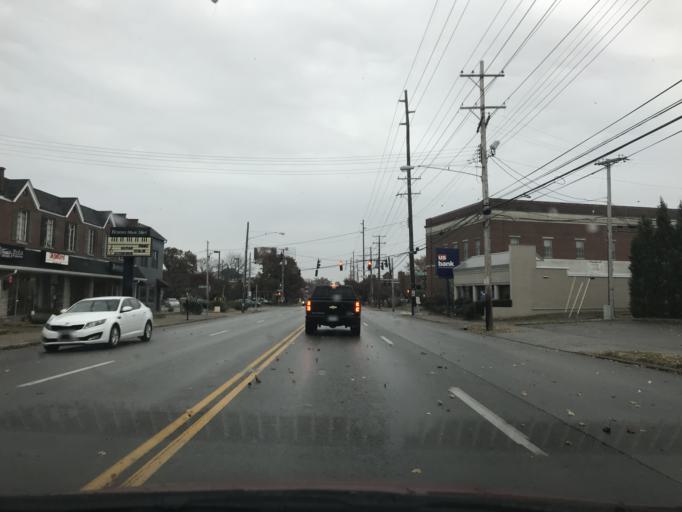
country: US
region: Kentucky
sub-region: Jefferson County
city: West Buechel
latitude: 38.2239
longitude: -85.6900
